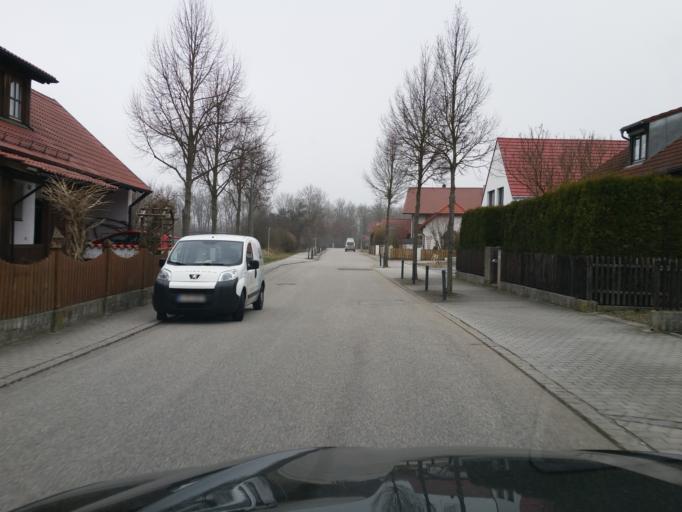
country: DE
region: Bavaria
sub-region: Lower Bavaria
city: Stallwang
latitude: 48.5700
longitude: 12.2129
